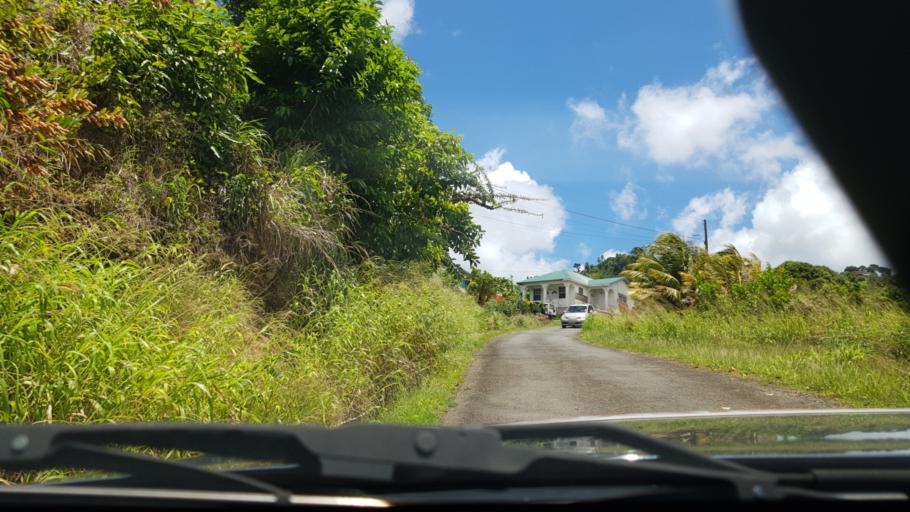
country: LC
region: Anse-la-Raye
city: Anse La Raye
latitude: 13.9523
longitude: -61.0007
